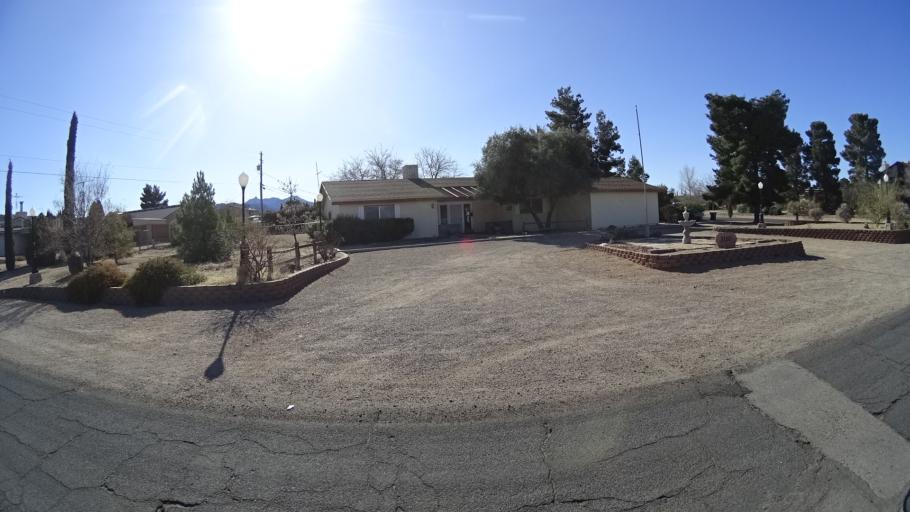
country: US
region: Arizona
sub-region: Mohave County
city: Kingman
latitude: 35.2065
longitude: -114.0089
